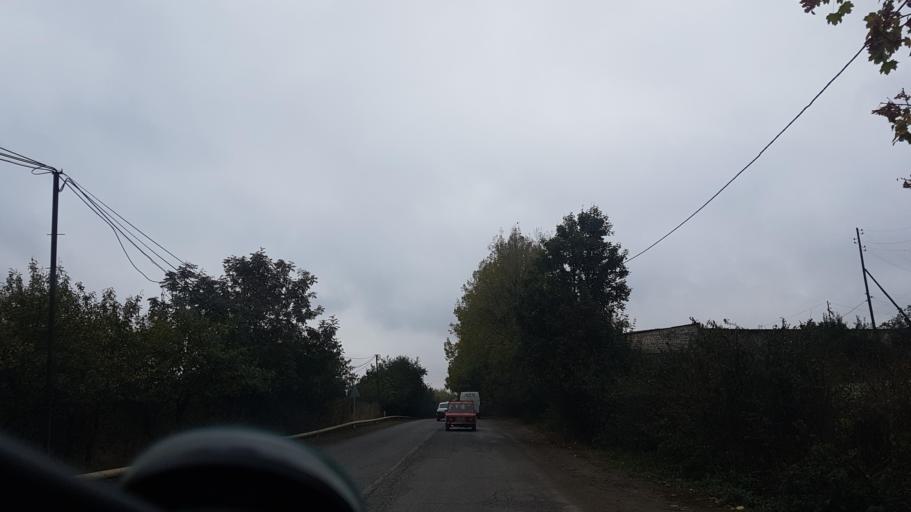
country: AZ
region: Gadabay Rayon
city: Ariqdam
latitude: 40.6541
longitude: 45.8067
